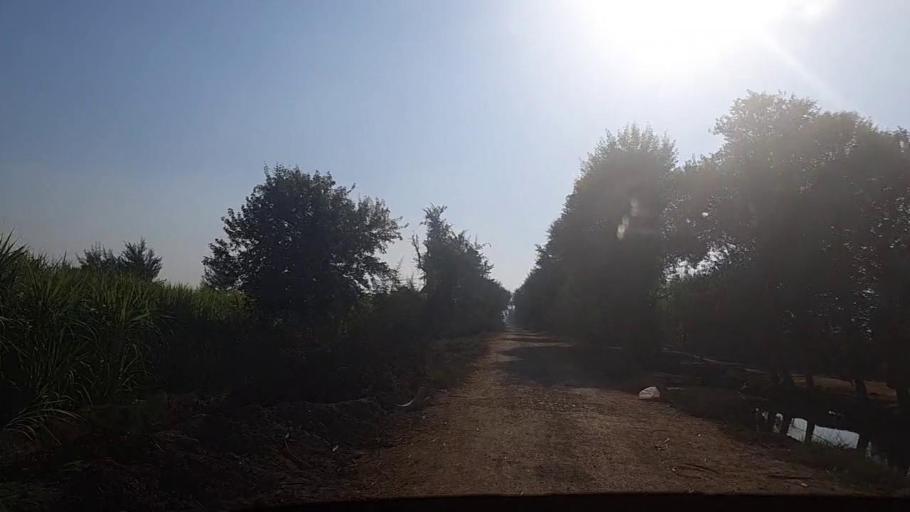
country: PK
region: Sindh
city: Gambat
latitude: 27.3754
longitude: 68.4664
